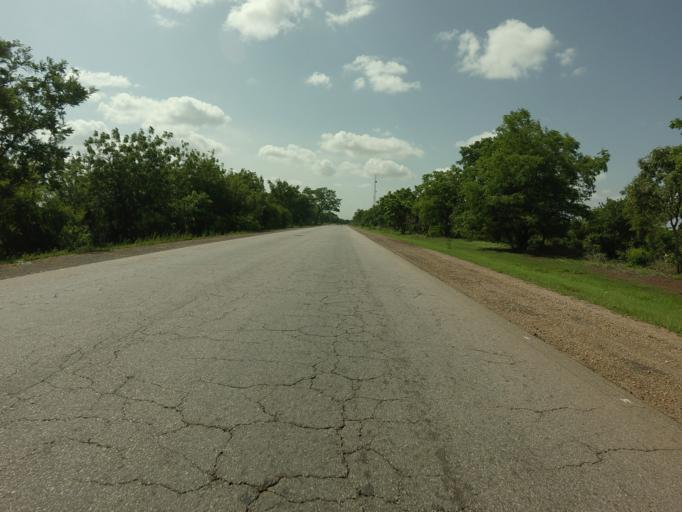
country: GH
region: Northern
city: Savelugu
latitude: 9.8135
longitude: -0.8616
